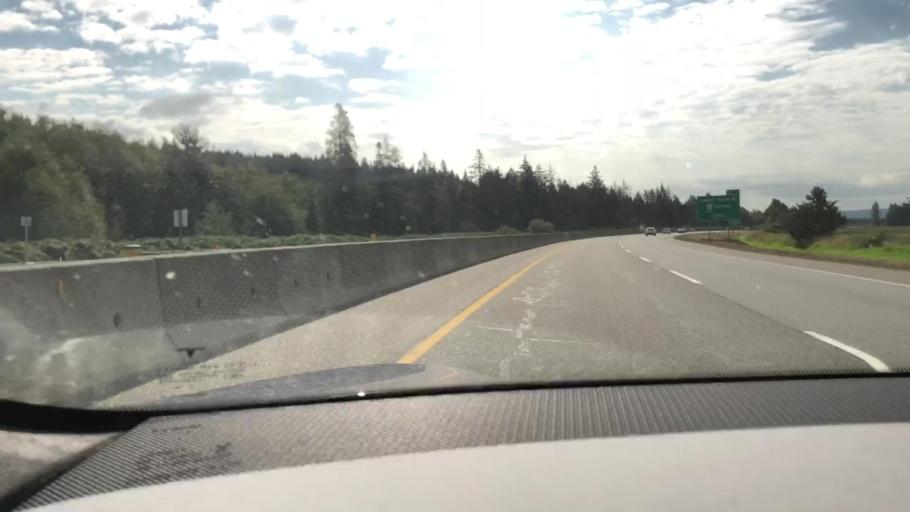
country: CA
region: British Columbia
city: Delta
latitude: 49.1113
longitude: -122.9071
